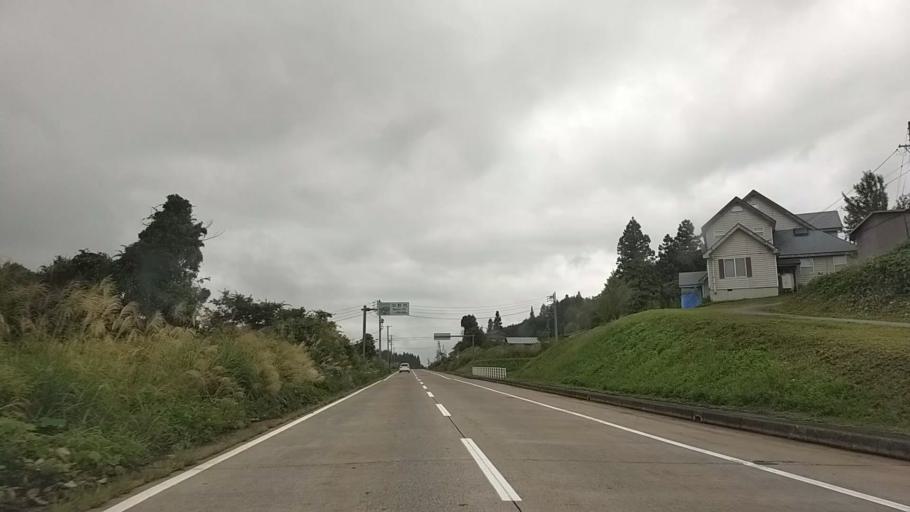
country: JP
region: Nagano
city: Iiyama
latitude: 36.8069
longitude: 138.3315
